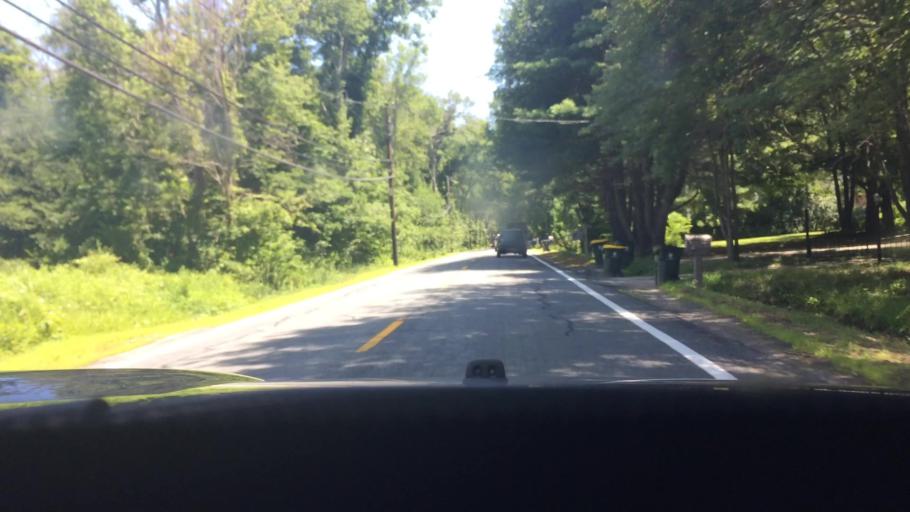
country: US
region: Rhode Island
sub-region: Providence County
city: Harrisville
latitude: 41.9688
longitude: -71.6514
